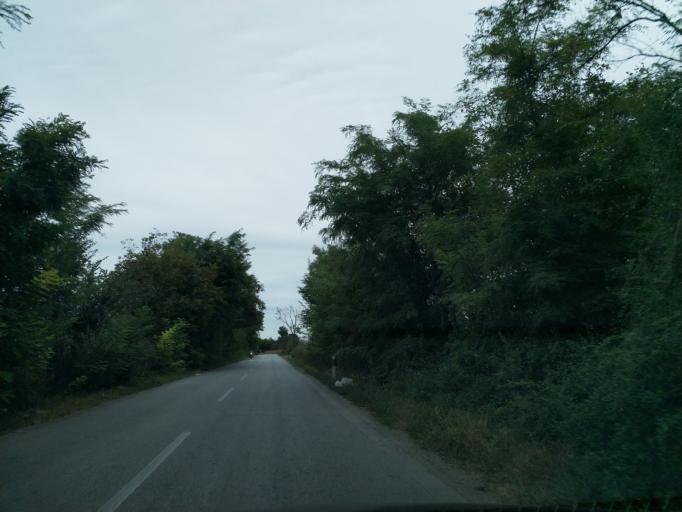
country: RS
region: Central Serbia
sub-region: Pomoravski Okrug
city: Paracin
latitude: 43.8402
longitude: 21.3733
